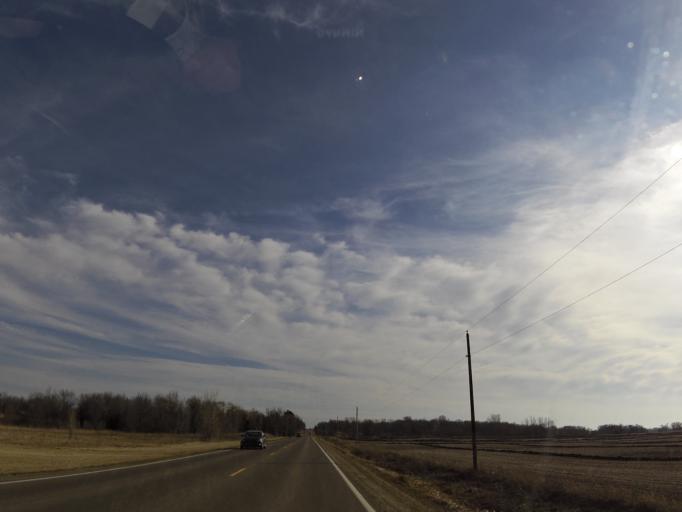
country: US
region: Minnesota
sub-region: Rice County
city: Northfield
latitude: 44.4968
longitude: -93.1999
